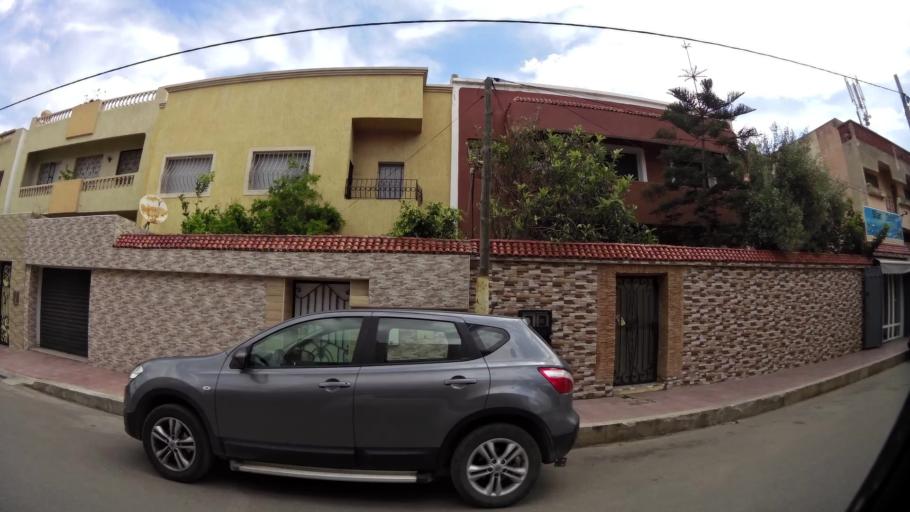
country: MA
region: Grand Casablanca
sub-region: Mediouna
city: Tit Mellil
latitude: 33.6177
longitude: -7.5344
